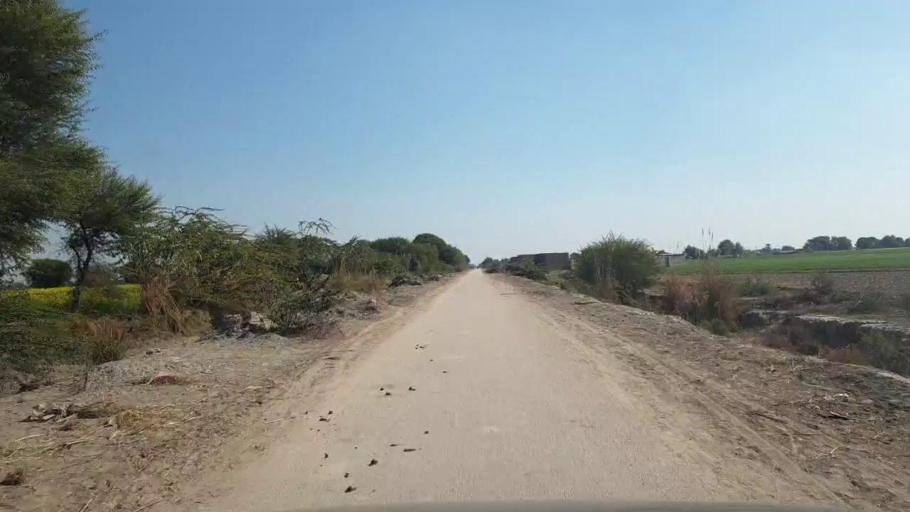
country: PK
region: Sindh
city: Shahpur Chakar
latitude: 26.1377
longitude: 68.6604
